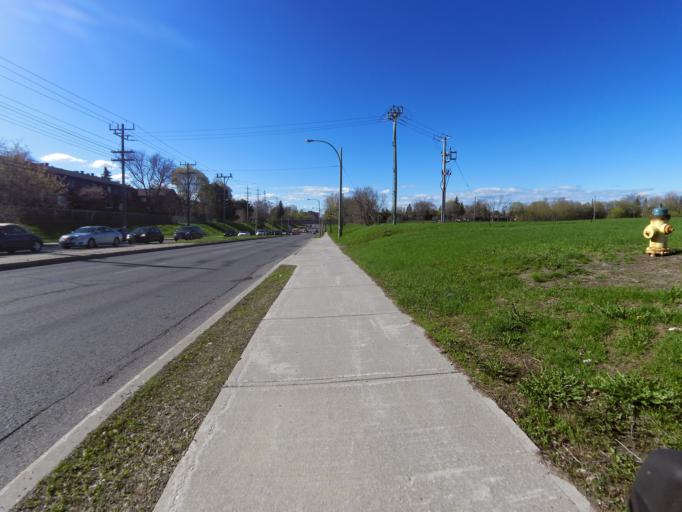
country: CA
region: Ontario
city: Bells Corners
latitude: 45.3322
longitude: -75.7828
